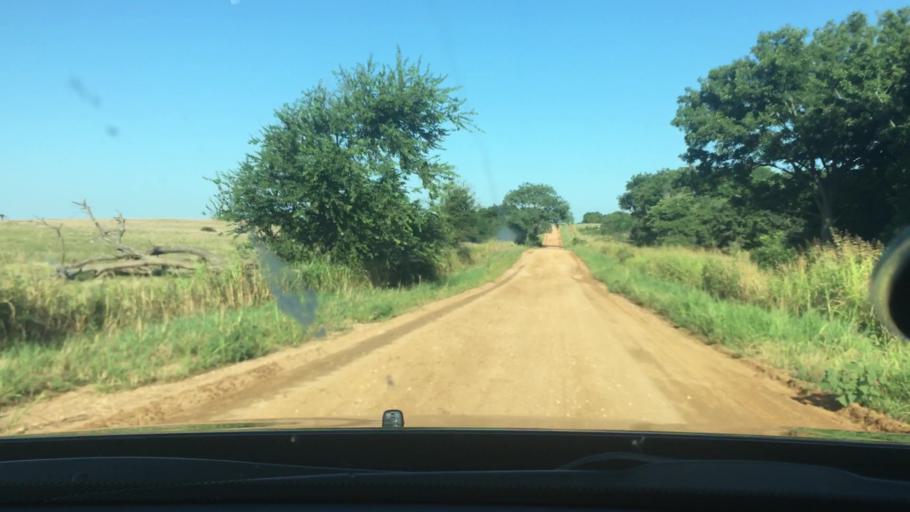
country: US
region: Oklahoma
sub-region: Johnston County
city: Tishomingo
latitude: 34.4195
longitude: -96.7786
